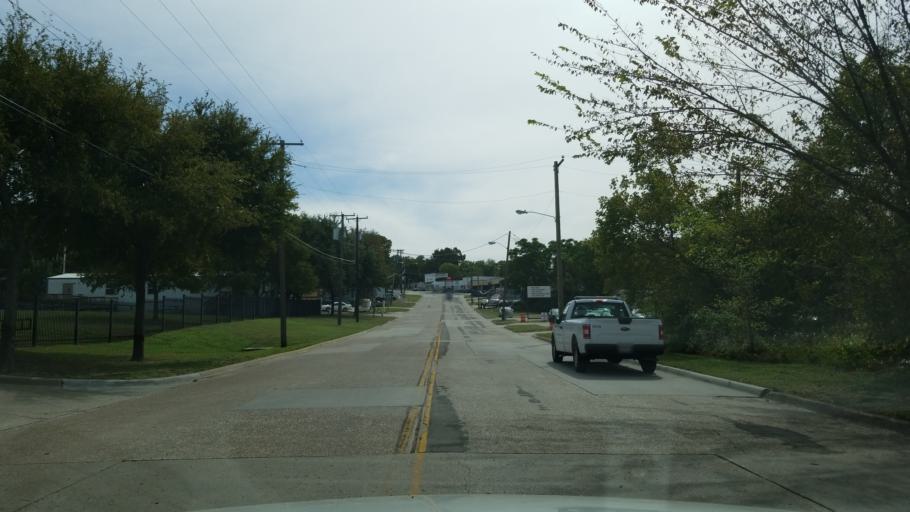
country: US
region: Texas
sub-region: Dallas County
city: Dallas
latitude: 32.7858
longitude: -96.7232
